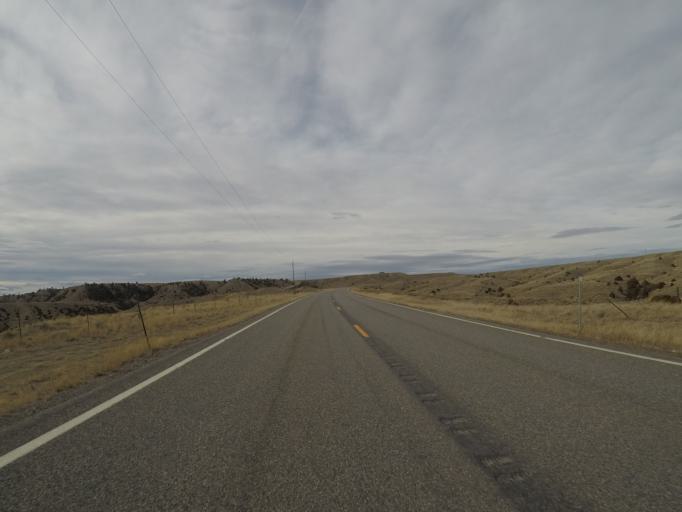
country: US
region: Montana
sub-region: Yellowstone County
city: Laurel
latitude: 45.8501
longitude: -108.7467
